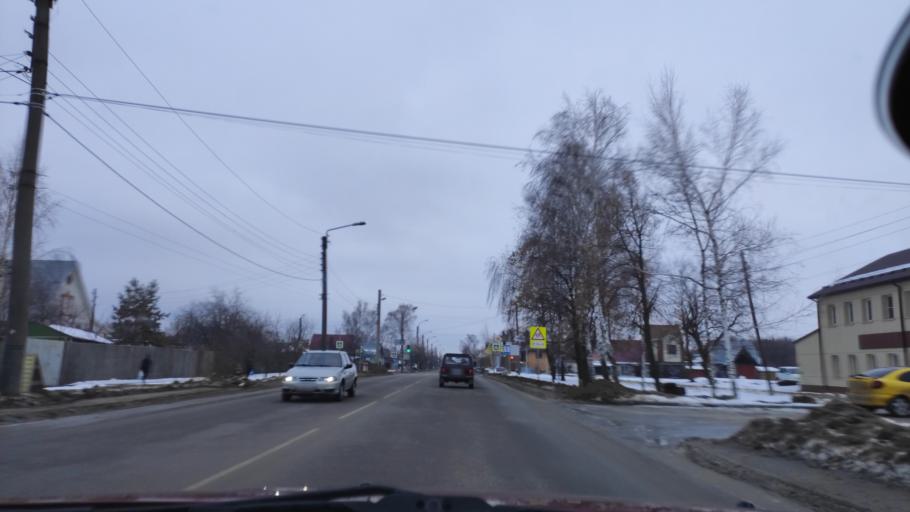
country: RU
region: Tambov
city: Tambov
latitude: 52.7130
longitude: 41.4408
